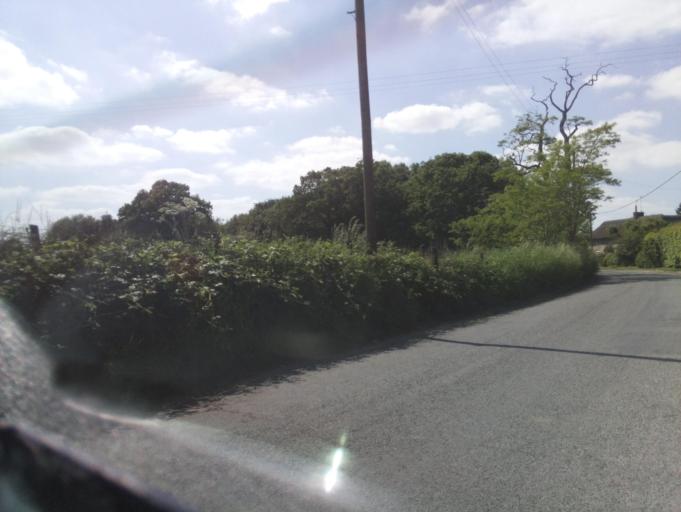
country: GB
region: England
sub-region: Wiltshire
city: Huish
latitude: 51.3527
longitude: -1.8021
